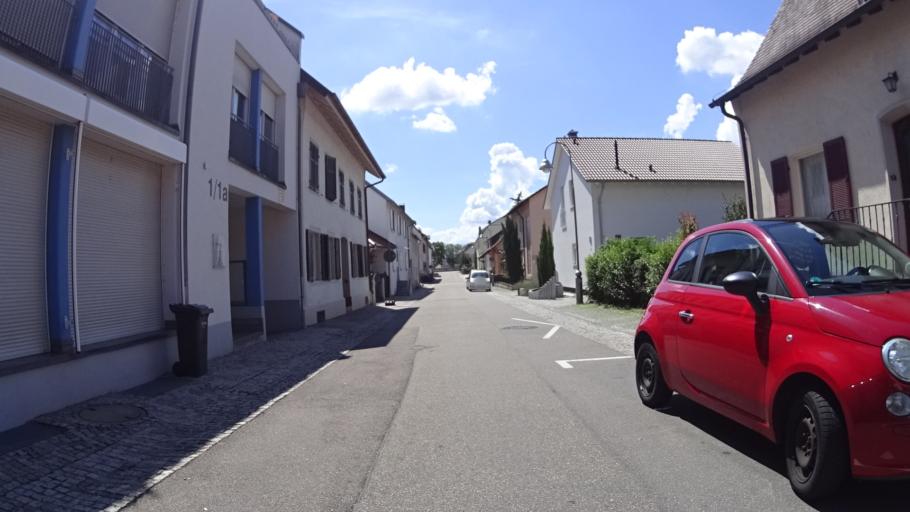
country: DE
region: Baden-Wuerttemberg
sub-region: Freiburg Region
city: Neuenburg am Rhein
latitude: 47.8133
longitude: 7.5620
